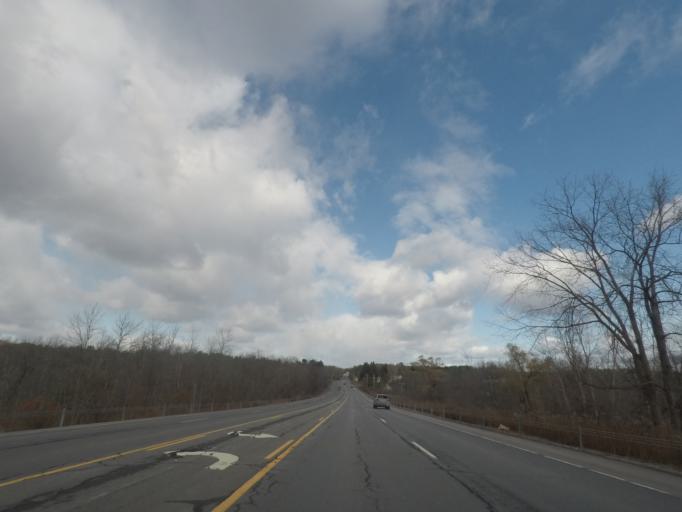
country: US
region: New York
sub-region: Saratoga County
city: Ballston Spa
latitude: 42.9985
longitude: -73.7910
